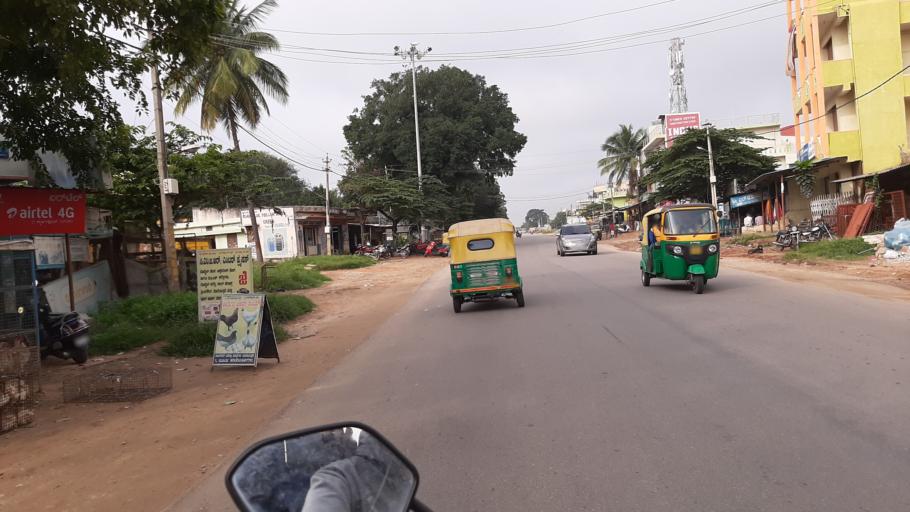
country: IN
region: Karnataka
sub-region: Bangalore Rural
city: Nelamangala
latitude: 12.9745
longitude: 77.4217
